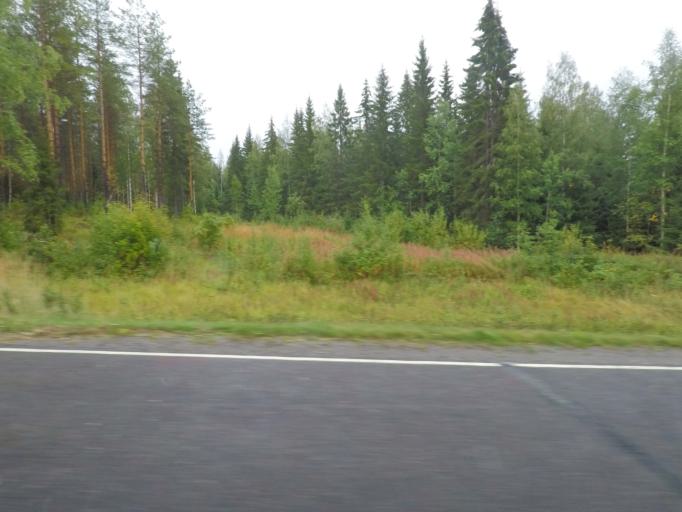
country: FI
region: Southern Savonia
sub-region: Pieksaemaeki
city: Joroinen
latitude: 62.1143
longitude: 27.8369
